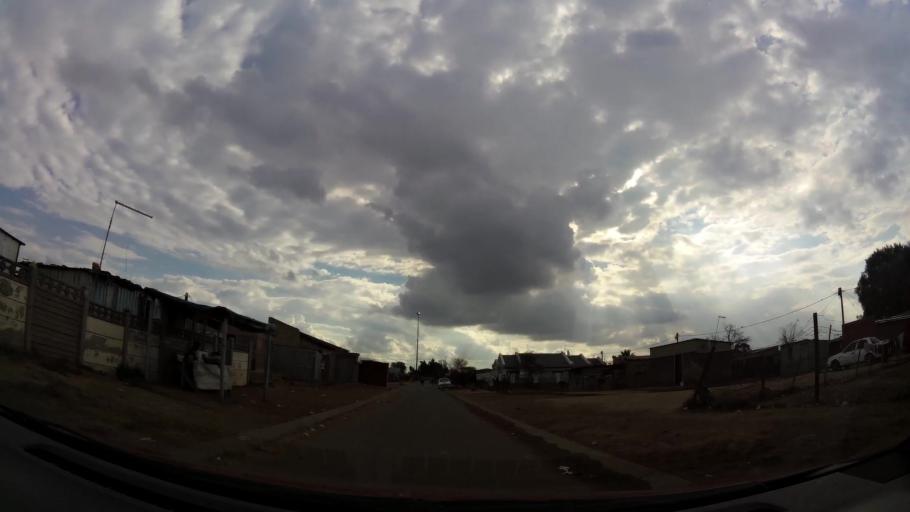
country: ZA
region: Gauteng
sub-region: Sedibeng District Municipality
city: Vanderbijlpark
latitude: -26.6751
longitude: 27.8583
